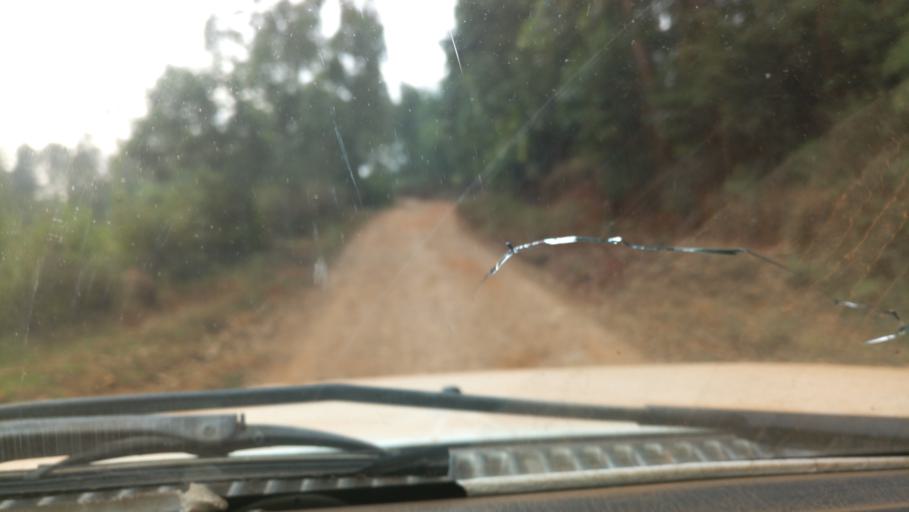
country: KE
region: Murang'a District
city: Kangema
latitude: -0.7143
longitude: 36.9973
